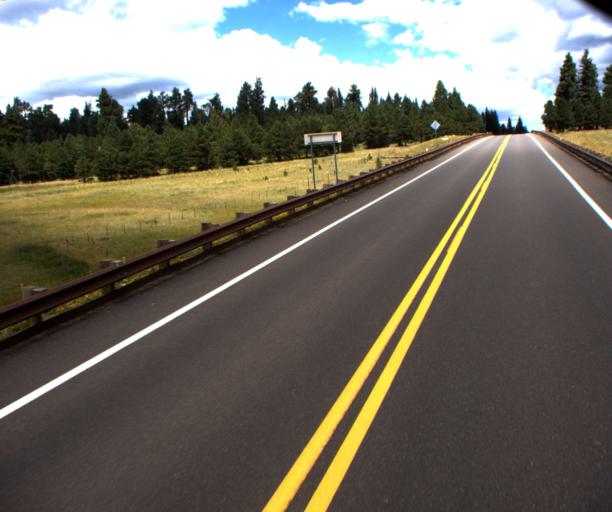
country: US
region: Arizona
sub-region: Apache County
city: Eagar
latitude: 33.9671
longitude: -109.4991
